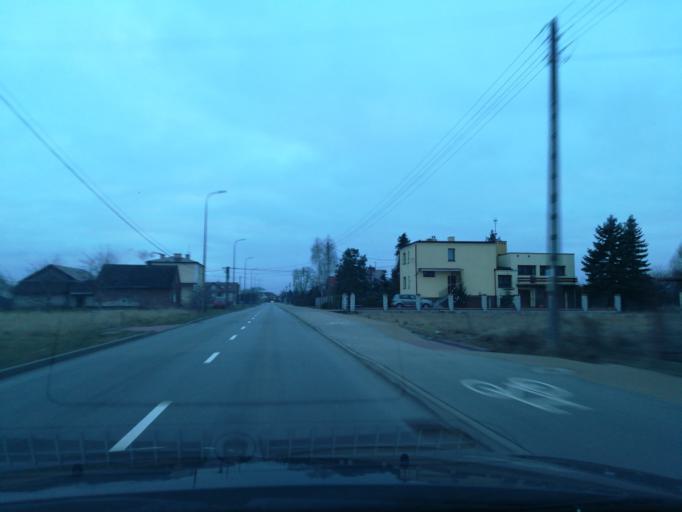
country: PL
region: Subcarpathian Voivodeship
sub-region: Rzeszow
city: Rzeszow
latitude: 50.0091
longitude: 22.0089
